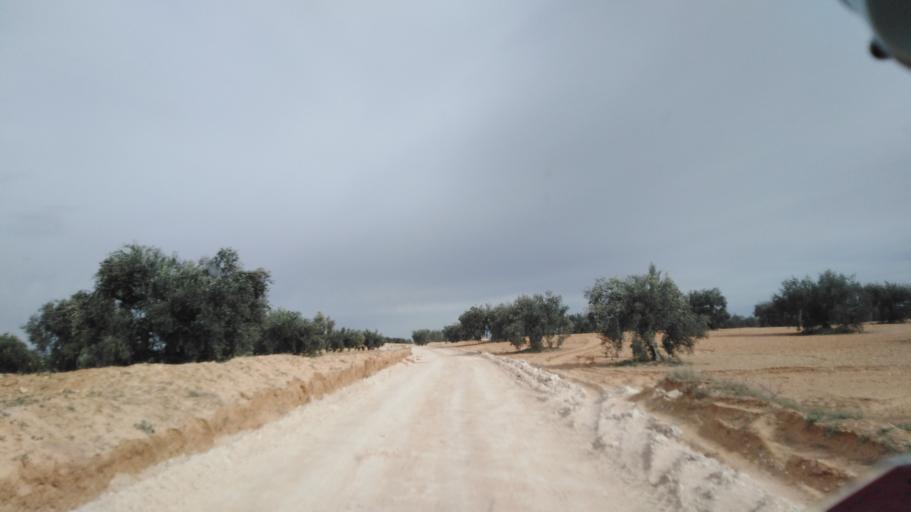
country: TN
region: Safaqis
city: Bi'r `Ali Bin Khalifah
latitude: 34.8119
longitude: 10.3064
